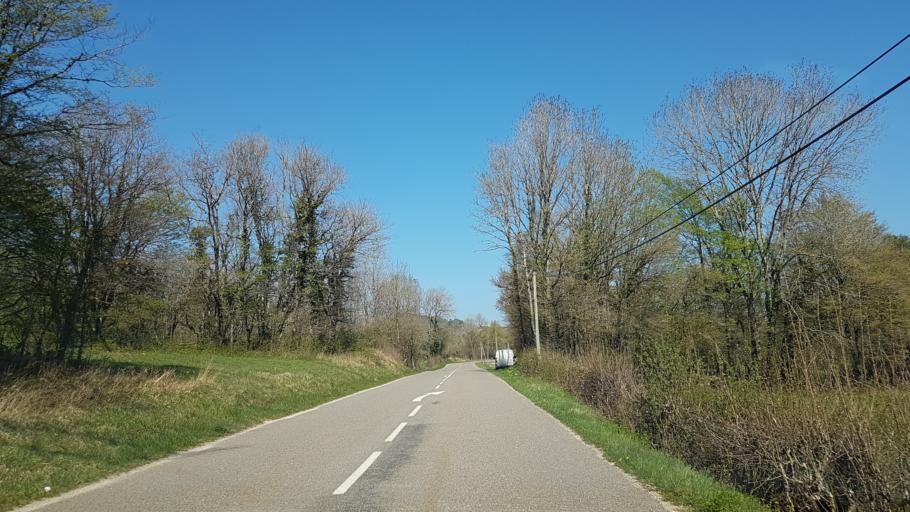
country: FR
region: Bourgogne
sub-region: Departement de Saone-et-Loire
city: Cuiseaux
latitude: 46.4602
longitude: 5.3990
